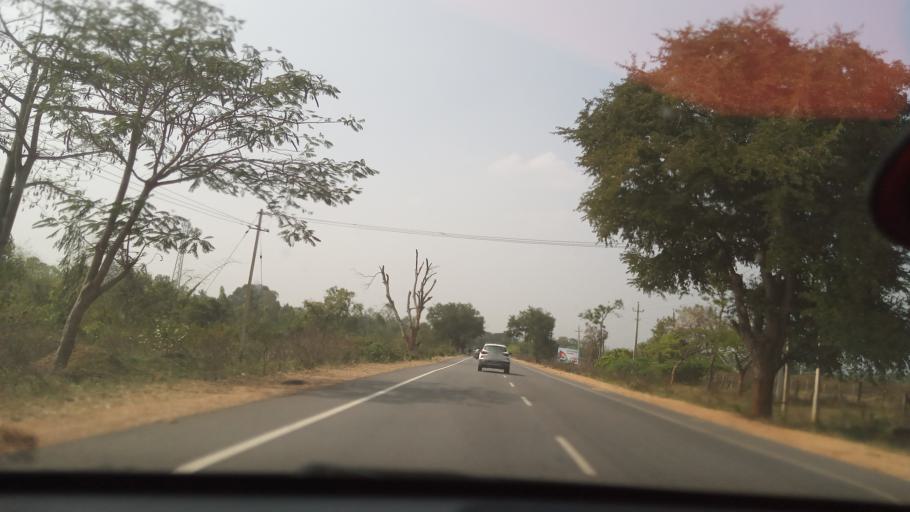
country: IN
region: Karnataka
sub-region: Mysore
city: Nanjangud
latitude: 12.1034
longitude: 76.7117
